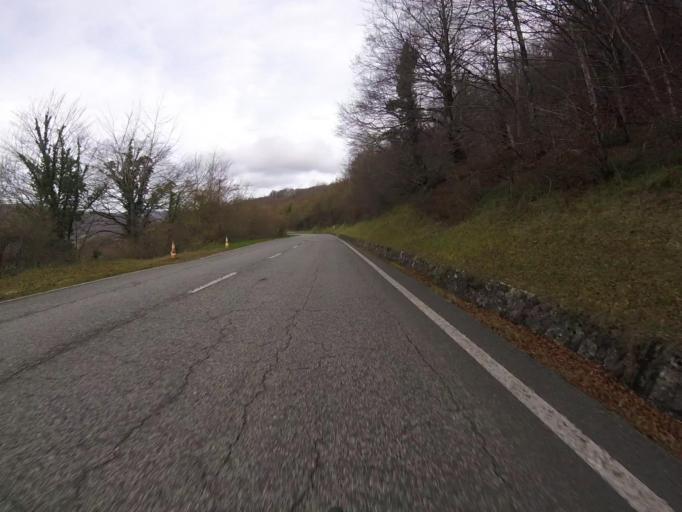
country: ES
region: Navarre
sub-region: Provincia de Navarra
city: Olazagutia
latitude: 42.8636
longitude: -2.1851
